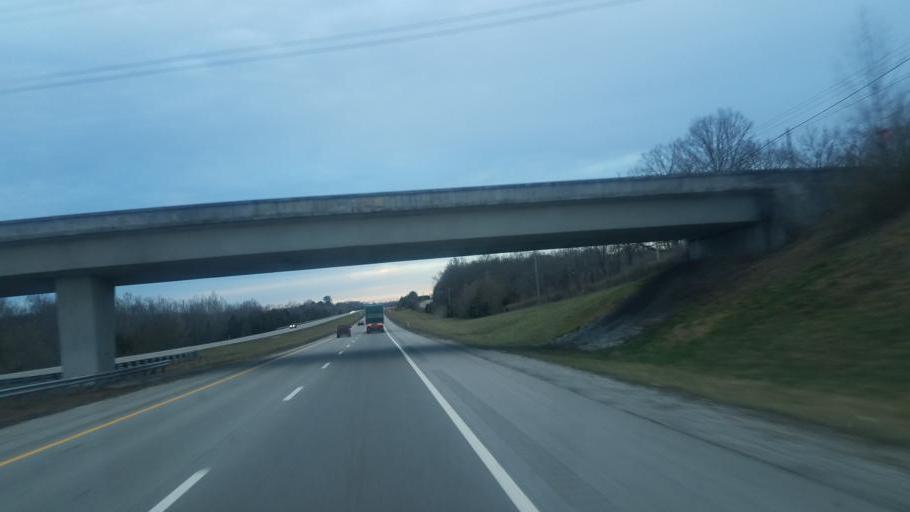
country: US
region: Tennessee
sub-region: Putnam County
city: Cookeville
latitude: 36.0876
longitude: -85.5057
